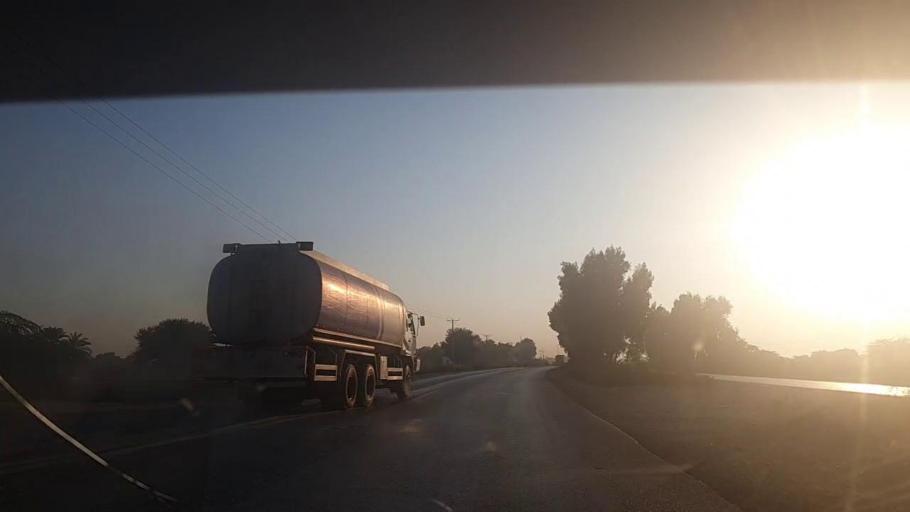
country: PK
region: Sindh
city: Hingorja
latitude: 27.1808
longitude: 68.3998
